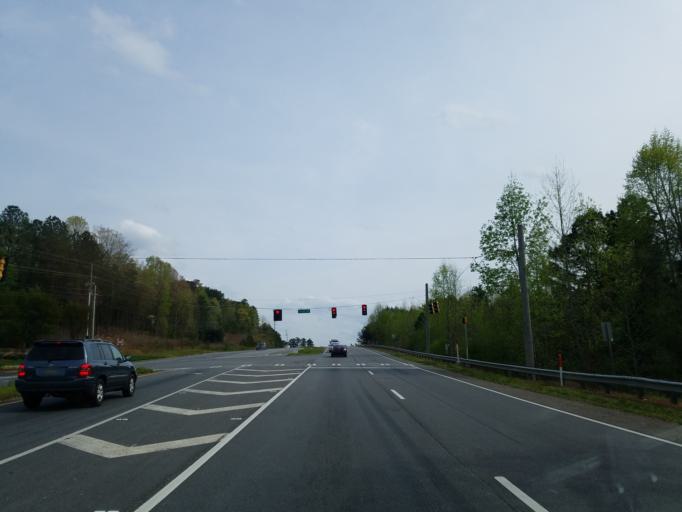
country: US
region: Georgia
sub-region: Fulton County
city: Johns Creek
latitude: 34.1059
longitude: -84.2173
